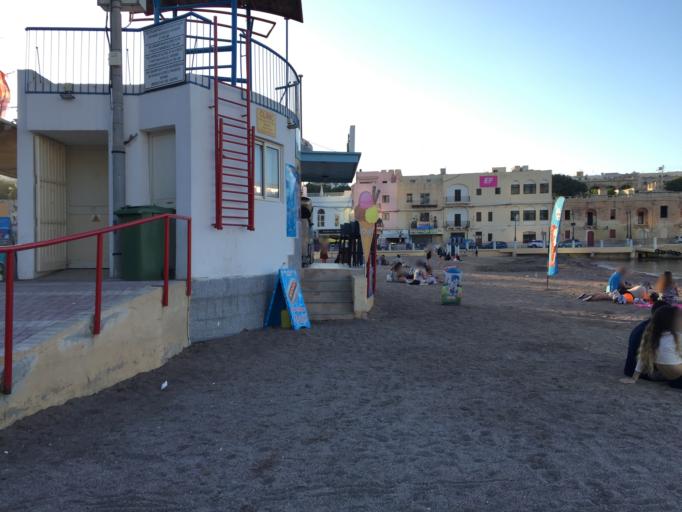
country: MT
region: Saint Julian
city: San Giljan
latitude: 35.9257
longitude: 14.4879
